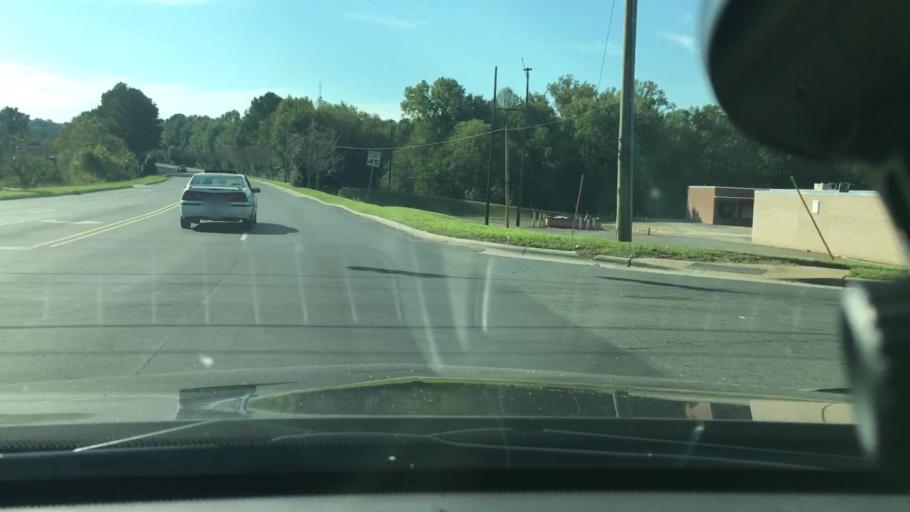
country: US
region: North Carolina
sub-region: Stanly County
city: Albemarle
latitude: 35.3460
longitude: -80.2041
